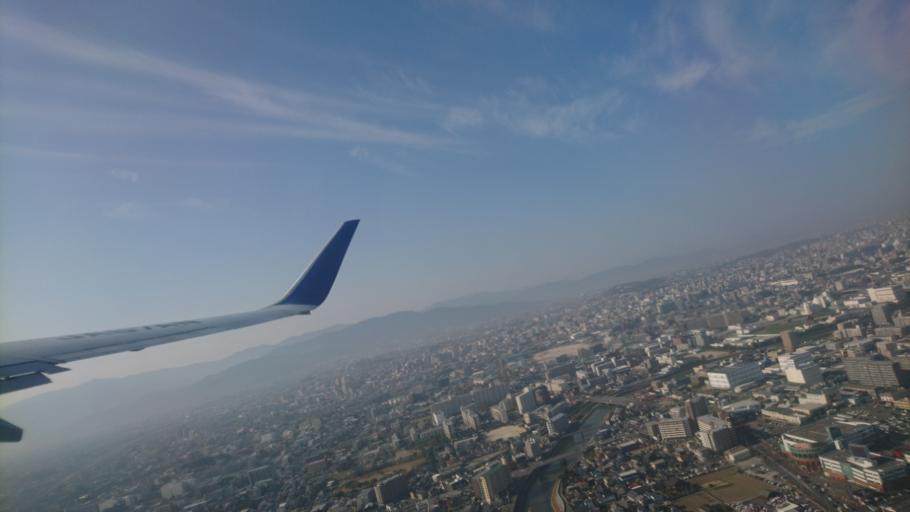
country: JP
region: Fukuoka
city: Onojo
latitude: 33.5711
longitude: 130.4622
